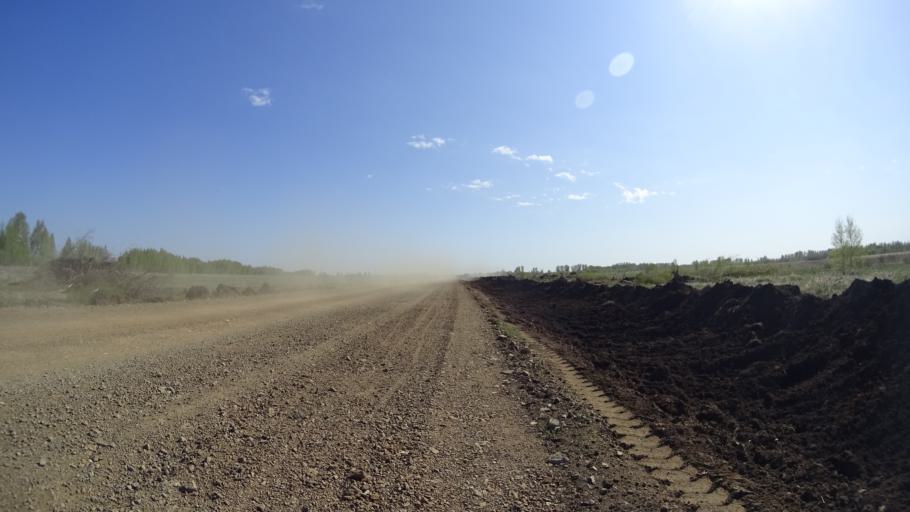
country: RU
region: Chelyabinsk
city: Troitsk
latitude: 54.1792
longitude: 61.4706
